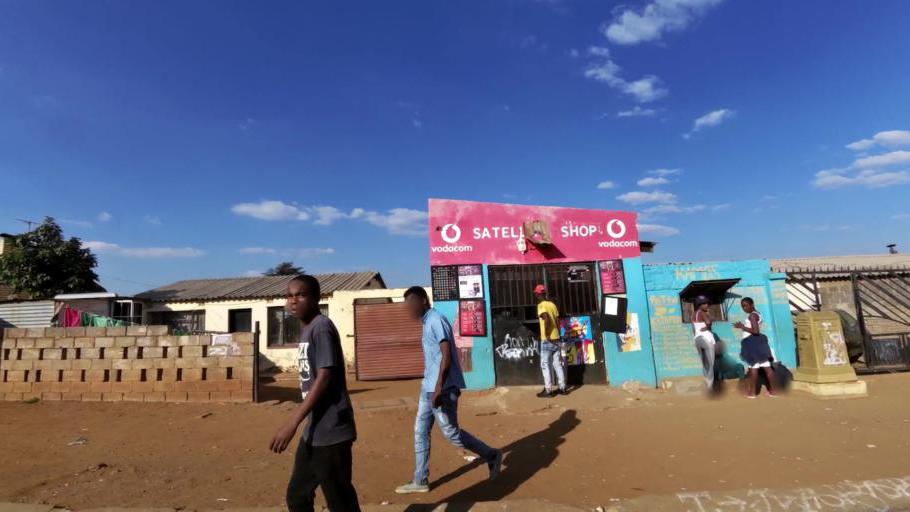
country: ZA
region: Gauteng
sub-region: City of Johannesburg Metropolitan Municipality
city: Roodepoort
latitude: -26.2160
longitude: 27.8747
